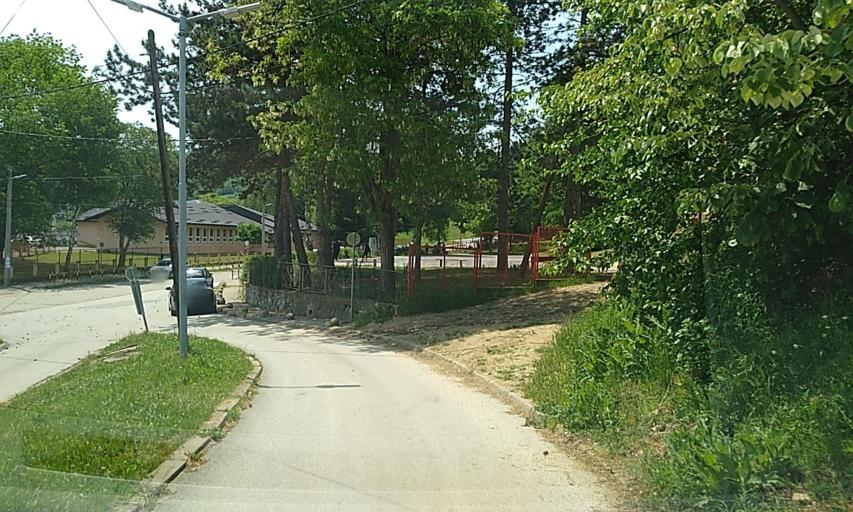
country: RS
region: Central Serbia
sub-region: Pcinjski Okrug
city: Vladicin Han
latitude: 42.7109
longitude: 22.0592
